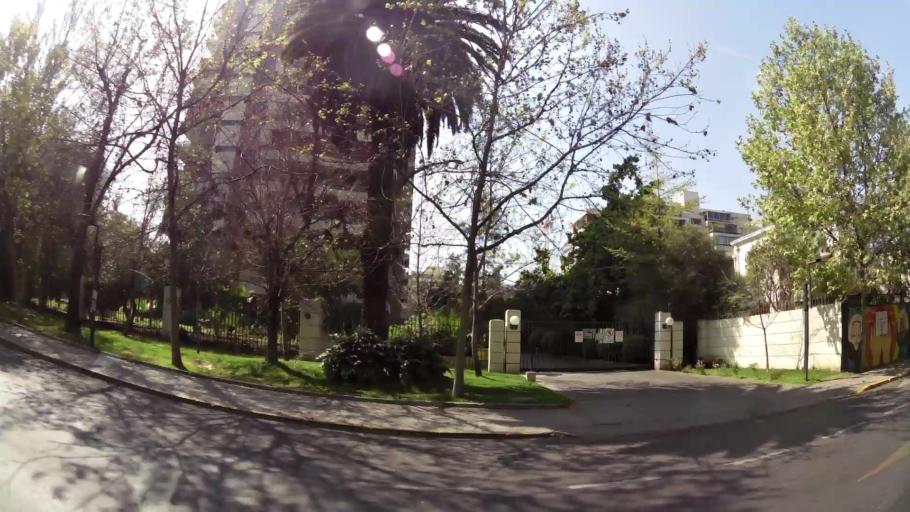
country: CL
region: Santiago Metropolitan
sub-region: Provincia de Santiago
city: Villa Presidente Frei, Nunoa, Santiago, Chile
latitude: -33.4350
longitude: -70.6014
